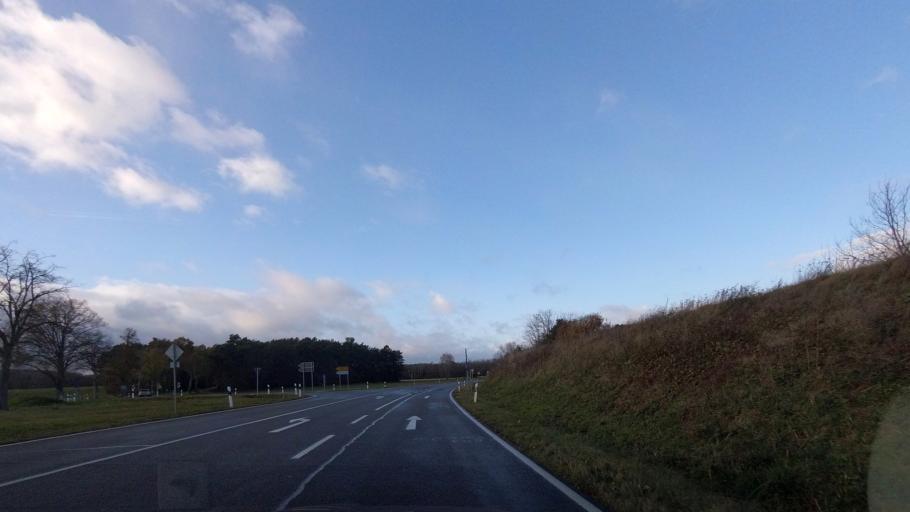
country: DE
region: Brandenburg
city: Belzig
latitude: 52.1323
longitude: 12.6261
